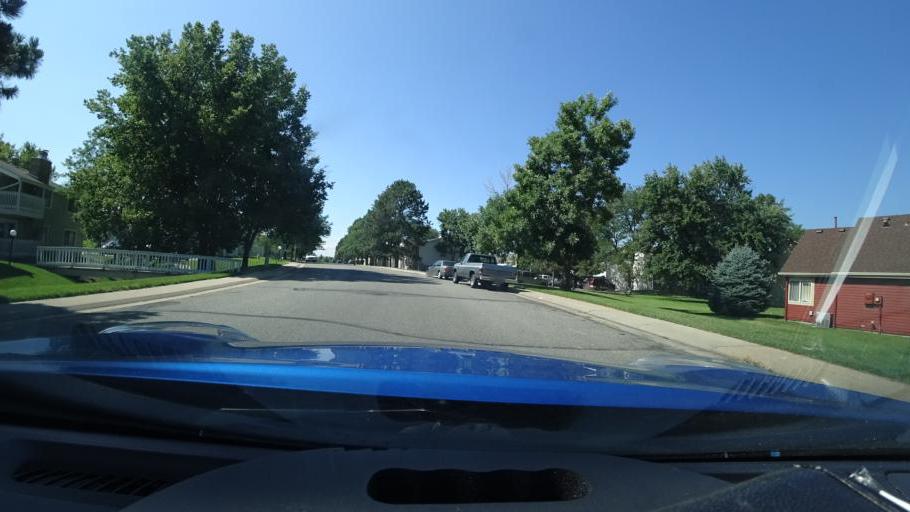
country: US
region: Colorado
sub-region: Adams County
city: Aurora
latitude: 39.6842
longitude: -104.8234
